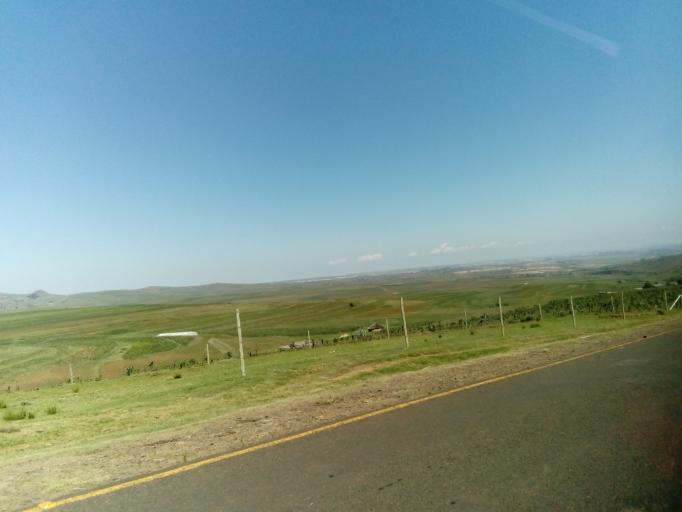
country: LS
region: Berea
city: Teyateyaneng
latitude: -29.2265
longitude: 27.8641
